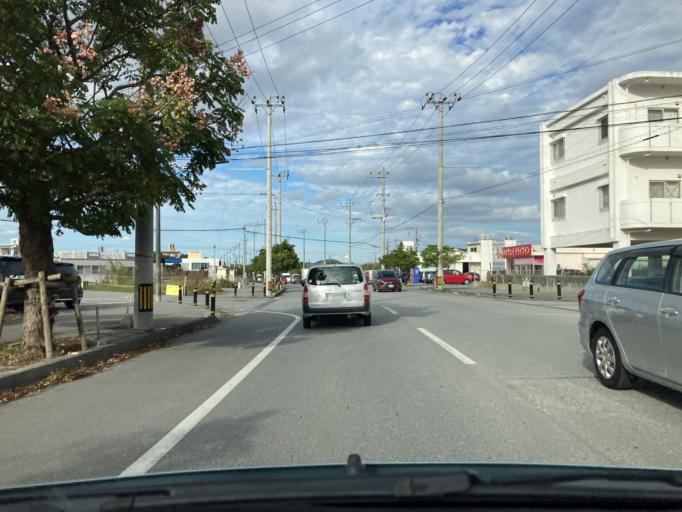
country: JP
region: Okinawa
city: Okinawa
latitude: 26.3698
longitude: 127.8263
